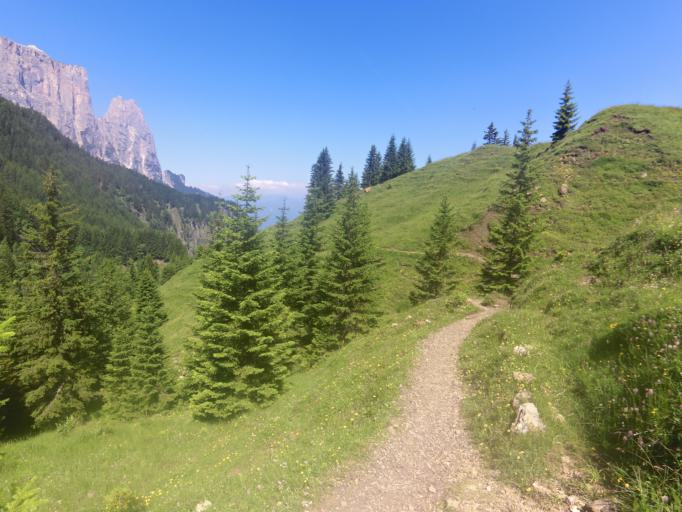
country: IT
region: Trentino-Alto Adige
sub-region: Bolzano
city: Siusi
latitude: 46.5156
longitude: 11.6029
